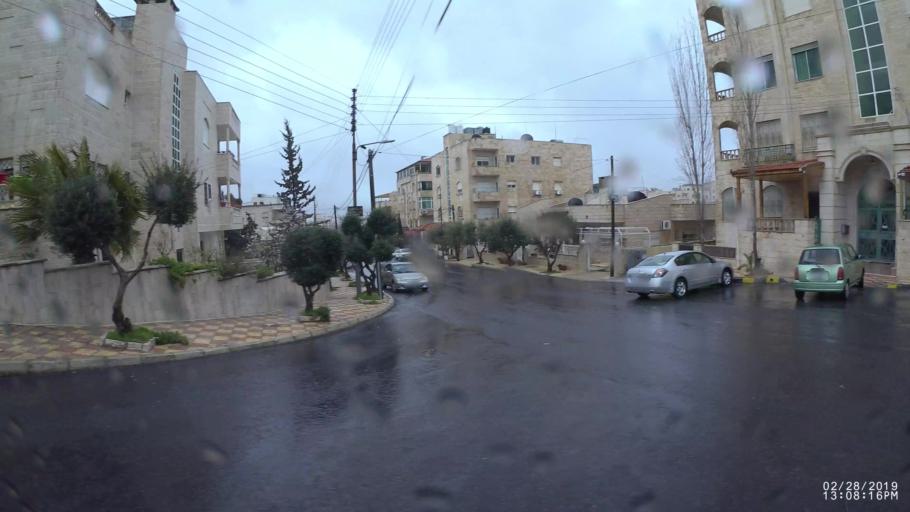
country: JO
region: Amman
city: Al Jubayhah
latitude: 32.0229
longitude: 35.8828
